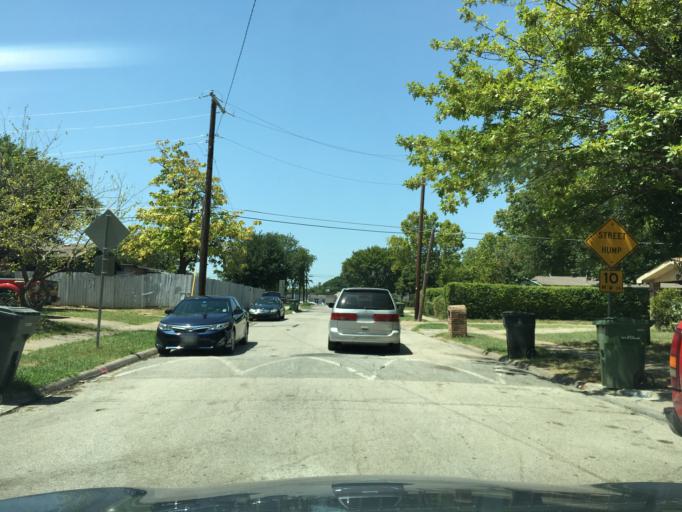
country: US
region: Texas
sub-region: Dallas County
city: Garland
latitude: 32.8960
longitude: -96.6289
